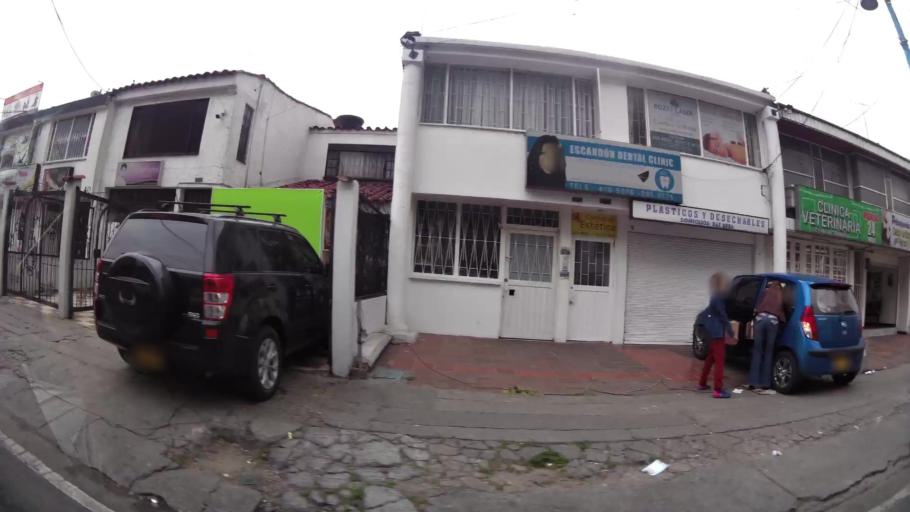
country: CO
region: Bogota D.C.
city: Bogota
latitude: 4.6679
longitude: -74.1178
